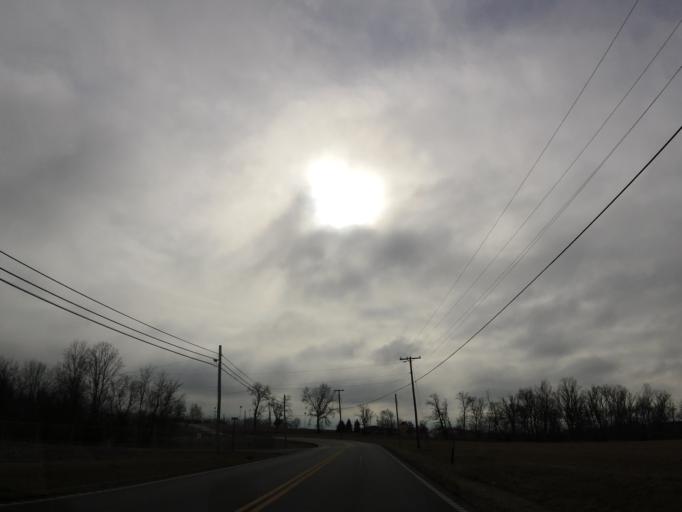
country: US
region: Kentucky
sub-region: Trimble County
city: Bedford
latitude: 38.6140
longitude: -85.3234
